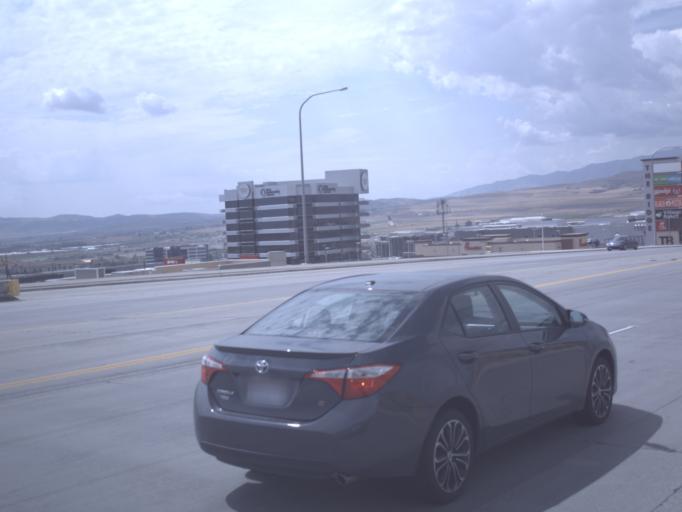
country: US
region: Utah
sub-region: Utah County
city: Lehi
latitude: 40.4317
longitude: -111.8844
